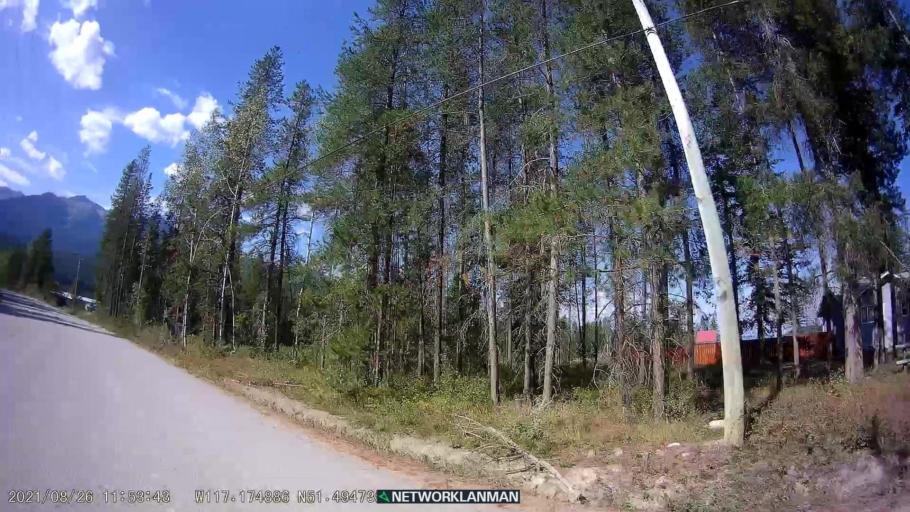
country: CA
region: British Columbia
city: Golden
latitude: 51.4943
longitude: -117.1755
